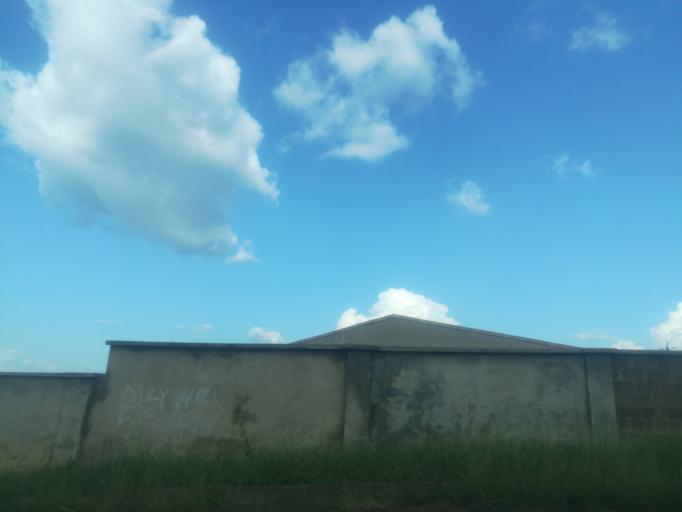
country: NG
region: Oyo
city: Ibadan
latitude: 7.4013
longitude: 3.9629
